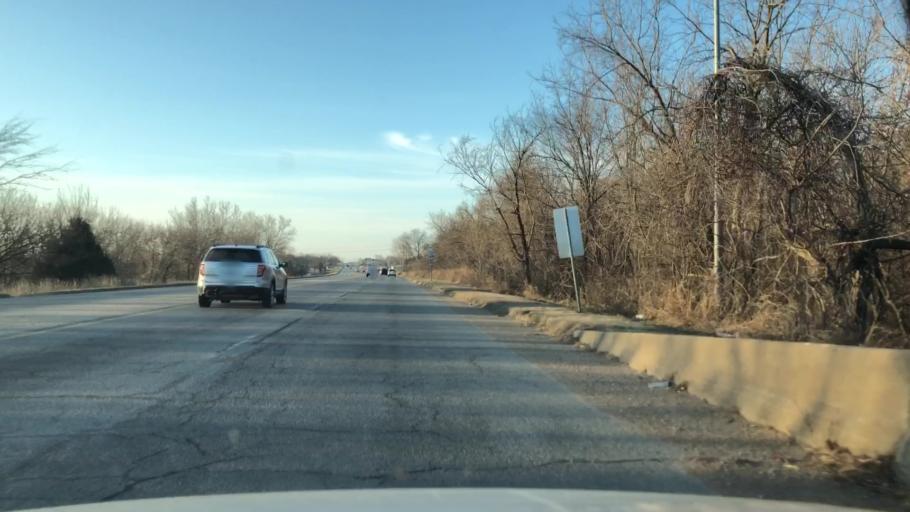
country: US
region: Oklahoma
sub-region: Washington County
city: Dewey
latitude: 36.7821
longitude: -95.9354
